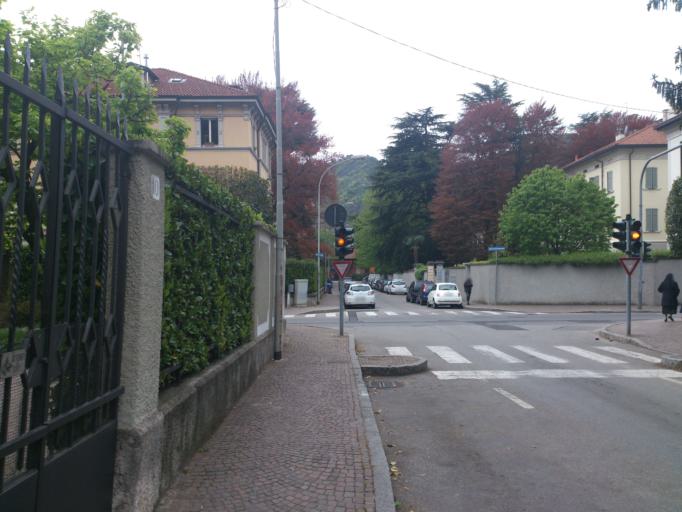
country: IT
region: Lombardy
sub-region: Provincia di Como
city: Como
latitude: 45.8064
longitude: 9.0926
